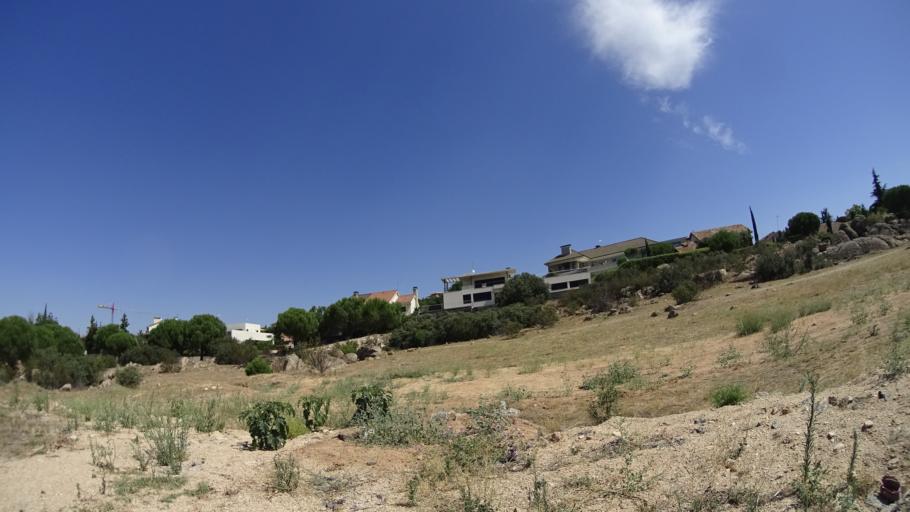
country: ES
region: Madrid
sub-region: Provincia de Madrid
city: Torrelodones
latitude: 40.5710
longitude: -3.9366
